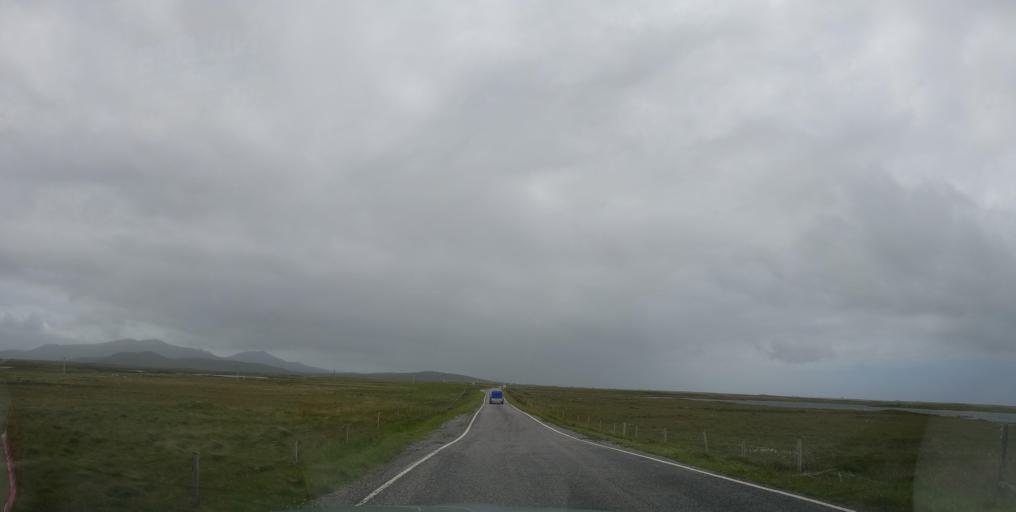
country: GB
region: Scotland
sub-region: Eilean Siar
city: Benbecula
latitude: 57.3757
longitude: -7.3449
